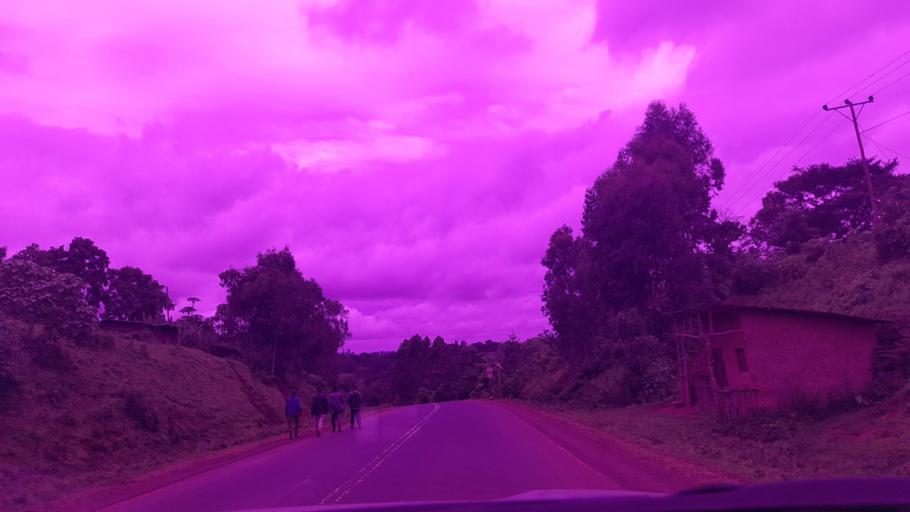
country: ET
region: Southern Nations, Nationalities, and People's Region
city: Bonga
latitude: 7.2935
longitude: 35.9841
